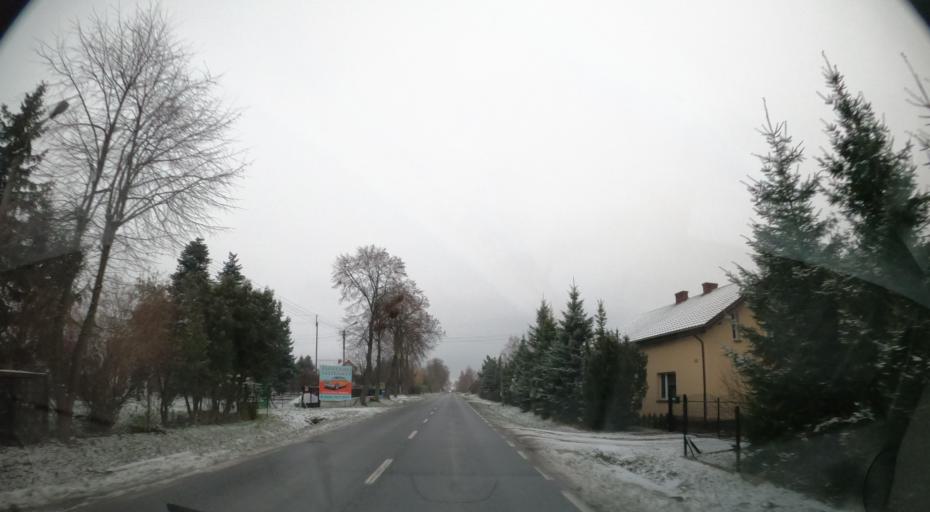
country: PL
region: Masovian Voivodeship
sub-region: Powiat plocki
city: Maszewo Duze
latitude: 52.5667
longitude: 19.6252
